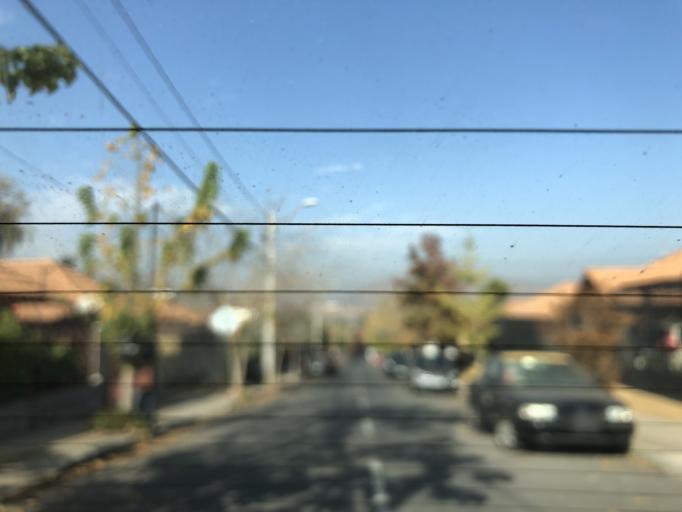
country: CL
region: Santiago Metropolitan
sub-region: Provincia de Cordillera
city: Puente Alto
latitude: -33.5926
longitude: -70.5369
